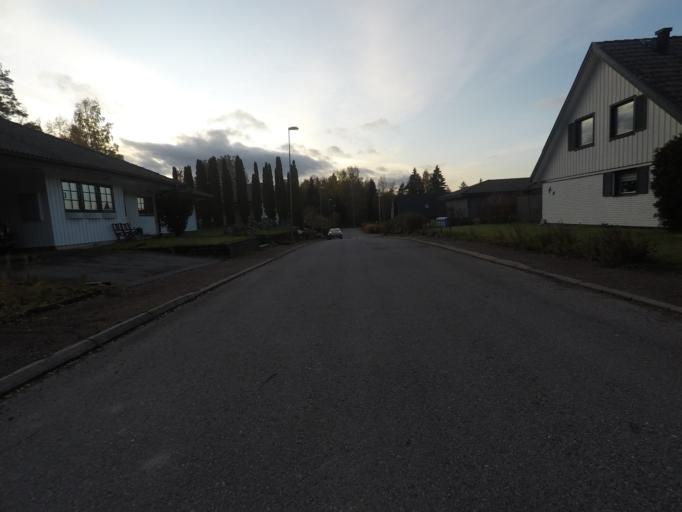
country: SE
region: OErebro
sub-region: Karlskoga Kommun
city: Karlskoga
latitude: 59.3073
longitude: 14.4783
